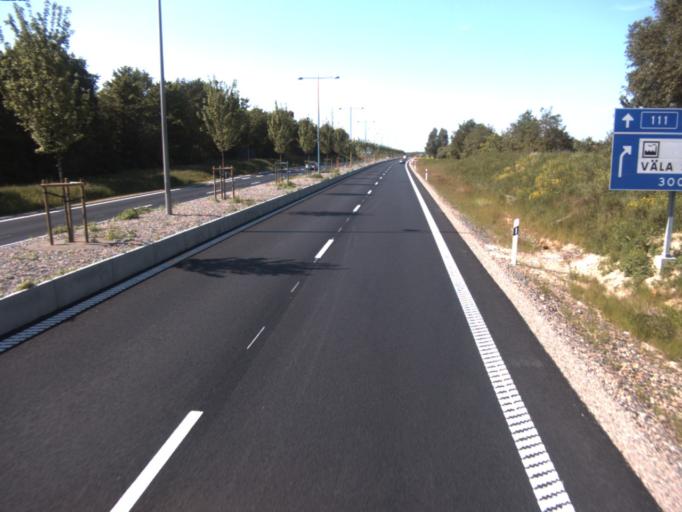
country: SE
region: Skane
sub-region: Helsingborg
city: Odakra
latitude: 56.0684
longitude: 12.7427
